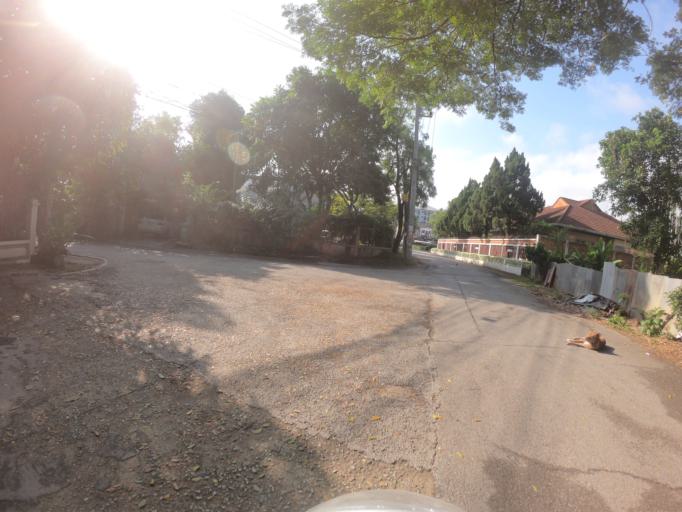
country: TH
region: Chiang Mai
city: Chiang Mai
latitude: 18.8133
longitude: 98.9662
